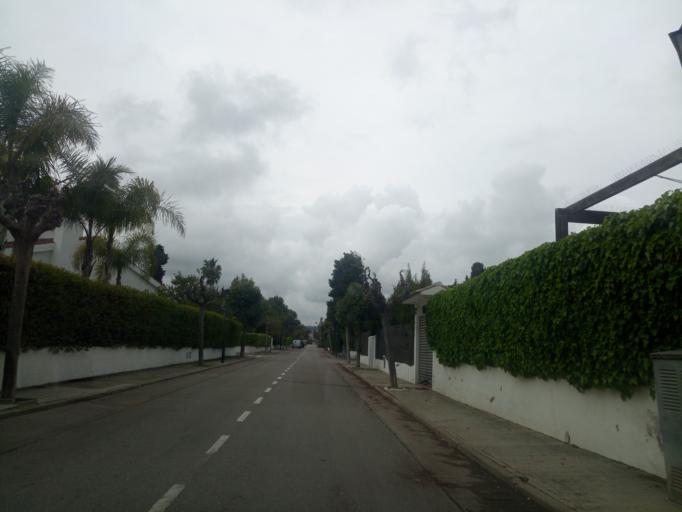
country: ES
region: Catalonia
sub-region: Provincia de Barcelona
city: Sant Pere de Ribes
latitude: 41.2523
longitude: 1.7799
